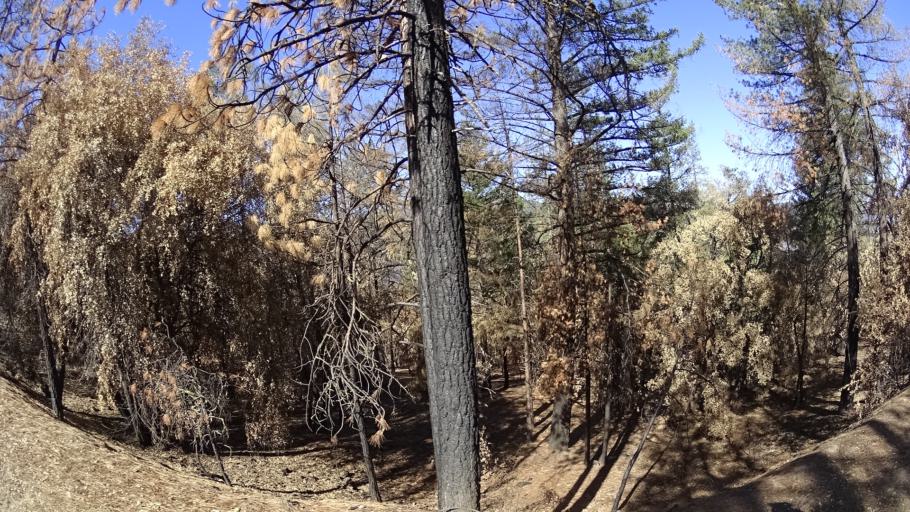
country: US
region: California
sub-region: Tehama County
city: Rancho Tehama Reserve
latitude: 39.6785
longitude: -122.7087
